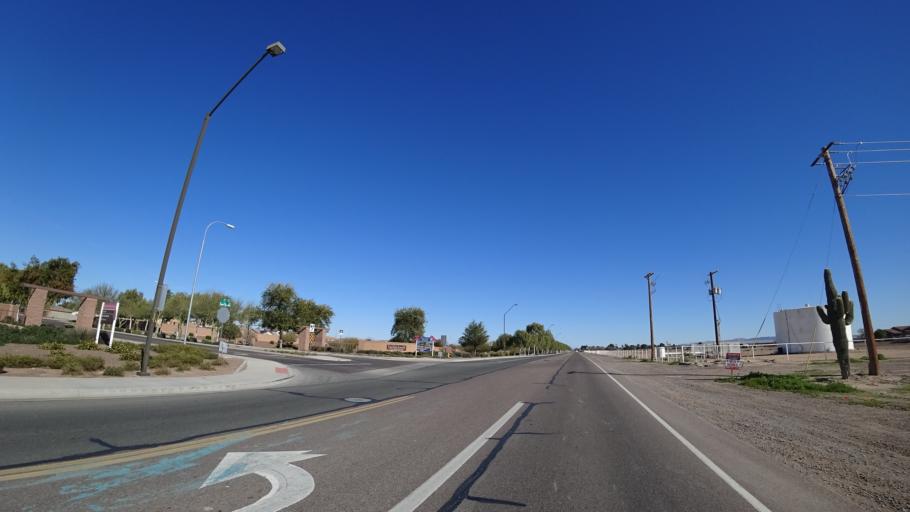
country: US
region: Arizona
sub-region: Maricopa County
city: Avondale
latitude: 33.4206
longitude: -112.3154
